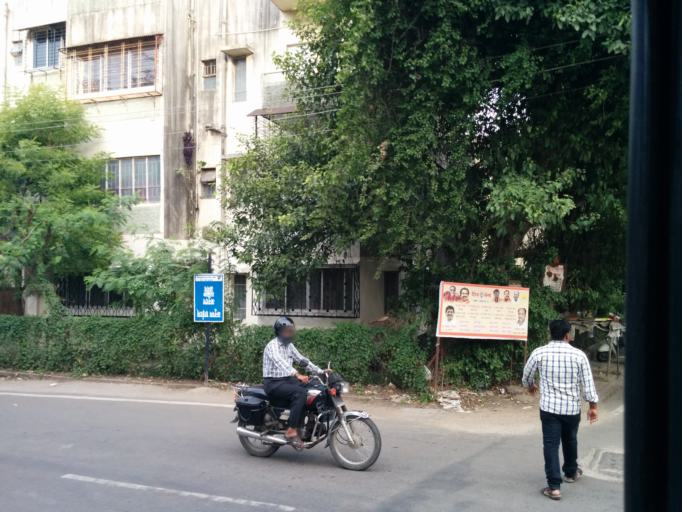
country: IN
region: Maharashtra
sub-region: Pune Division
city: Pune
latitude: 18.5113
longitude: 73.8156
